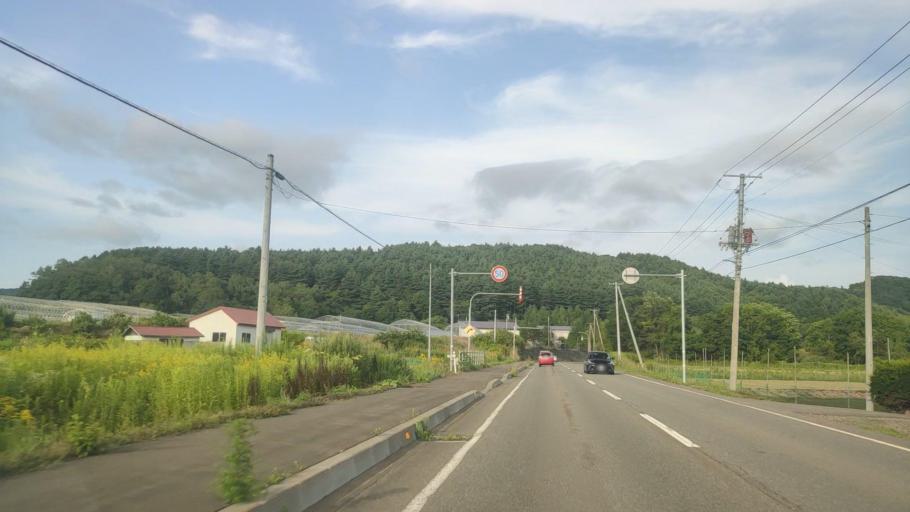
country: JP
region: Hokkaido
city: Iwamizawa
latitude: 43.0423
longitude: 141.9084
